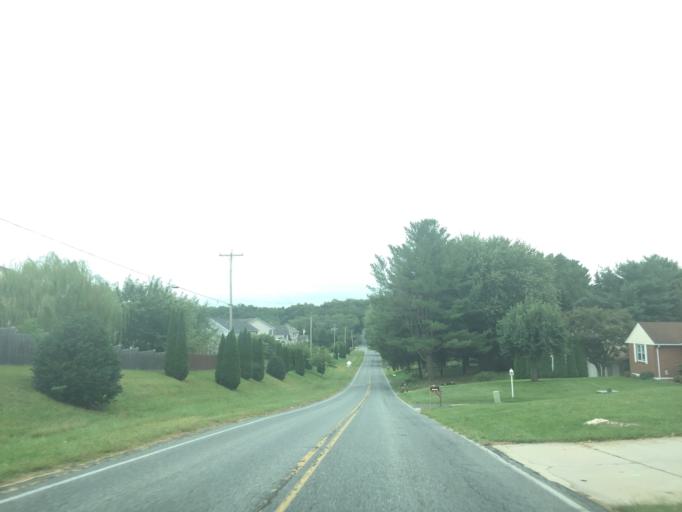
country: US
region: Maryland
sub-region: Harford County
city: Bel Air South
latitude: 39.5073
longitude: -76.3439
